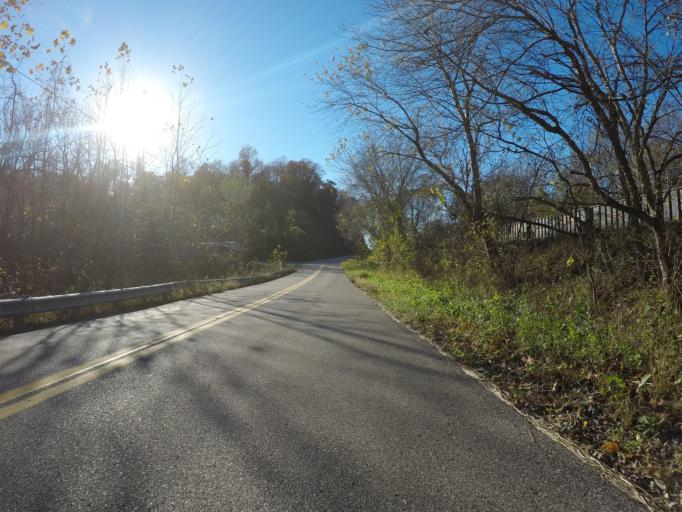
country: US
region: West Virginia
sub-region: Wayne County
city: Ceredo
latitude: 38.3931
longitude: -82.5487
